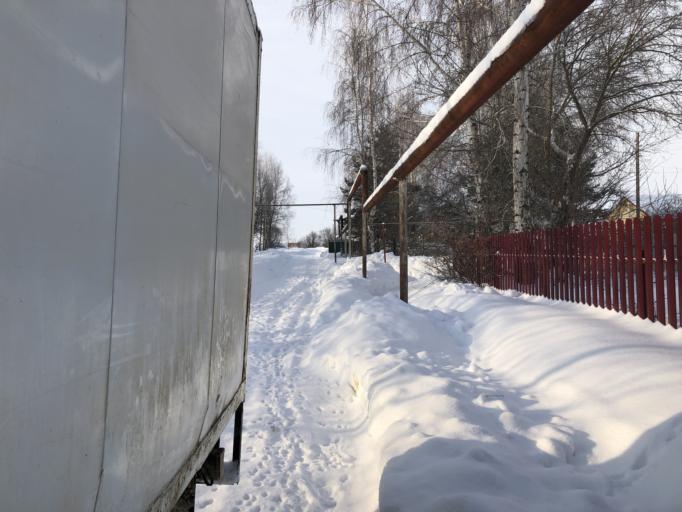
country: RU
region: Tula
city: Kimovsk
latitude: 53.9567
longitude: 38.7859
